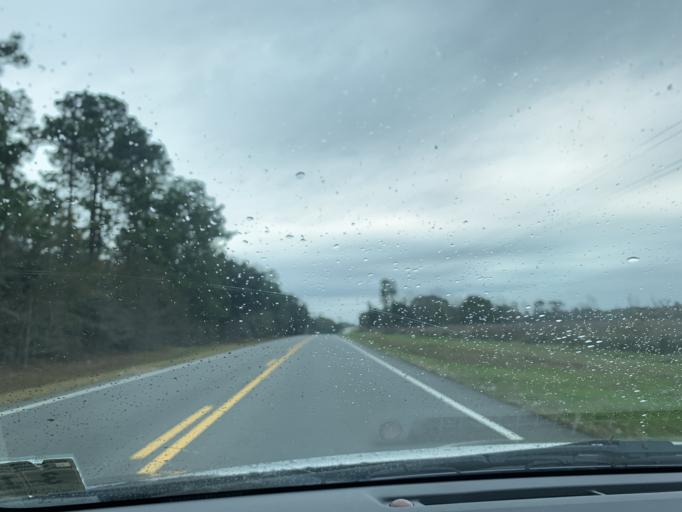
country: US
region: Georgia
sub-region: Grady County
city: Cairo
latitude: 30.9969
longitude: -84.2588
